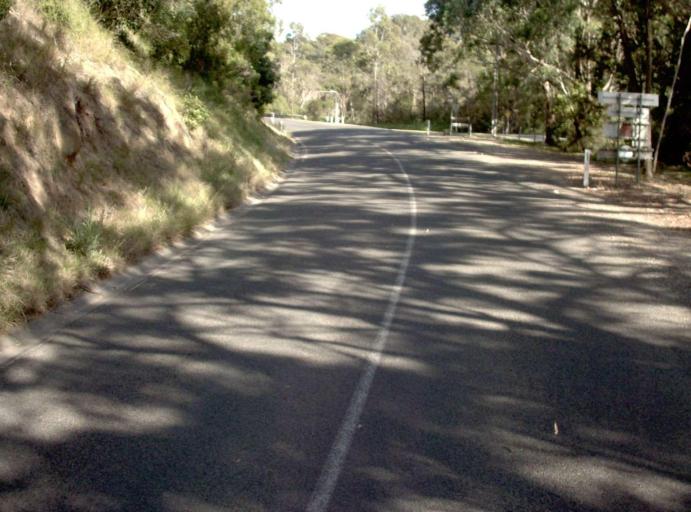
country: AU
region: Victoria
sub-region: East Gippsland
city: Lakes Entrance
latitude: -37.8793
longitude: 147.8584
